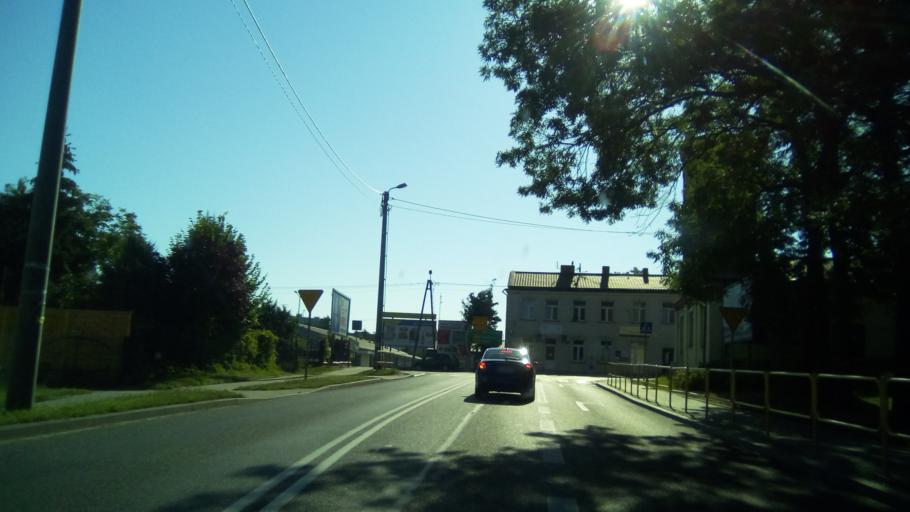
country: PL
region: Kujawsko-Pomorskie
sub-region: Powiat wloclawski
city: Brzesc Kujawski
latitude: 52.6068
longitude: 18.9007
